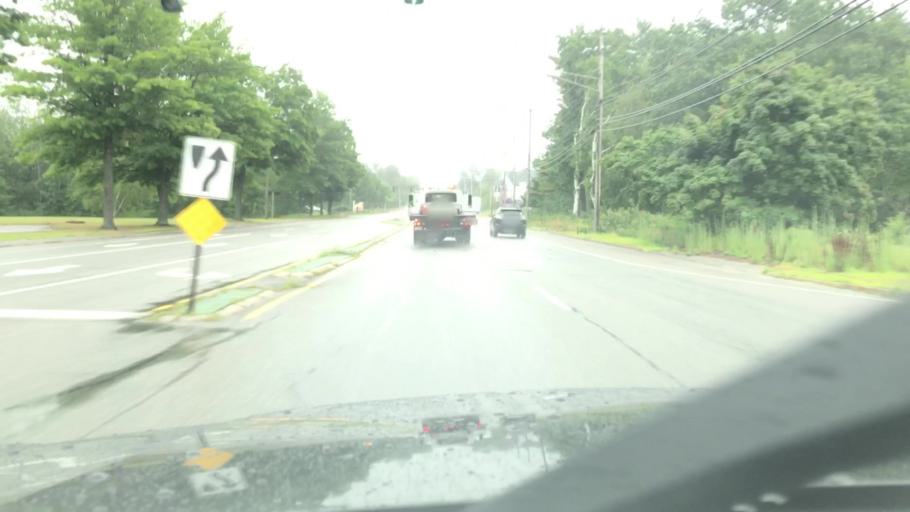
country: US
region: Maine
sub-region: Cumberland County
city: Scarborough
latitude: 43.5884
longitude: -70.3458
